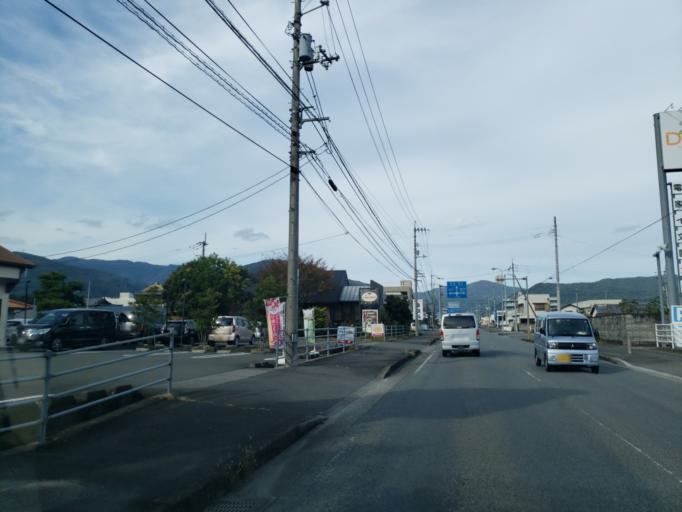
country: JP
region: Tokushima
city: Wakimachi
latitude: 34.0637
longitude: 134.1694
